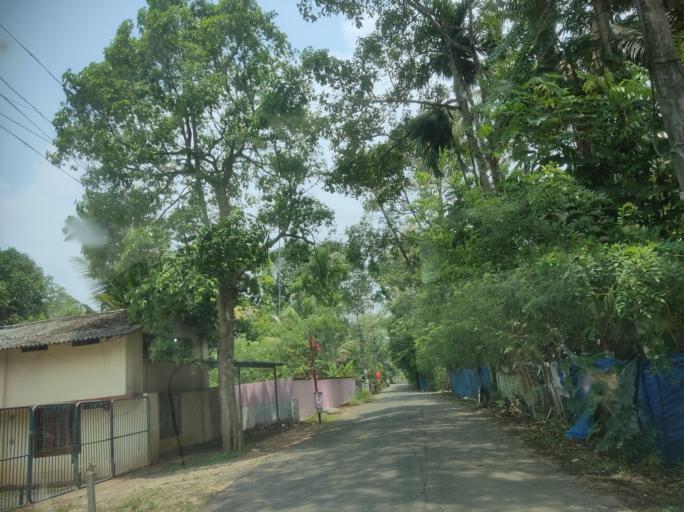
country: IN
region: Kerala
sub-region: Alappuzha
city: Vayalar
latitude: 9.7272
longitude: 76.3281
